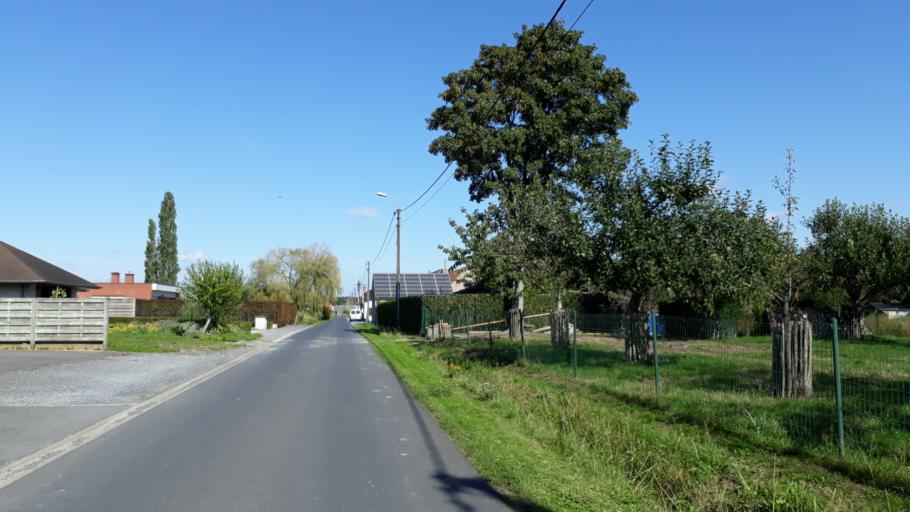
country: BE
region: Flanders
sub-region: Provincie West-Vlaanderen
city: Torhout
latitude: 51.0816
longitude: 3.1031
